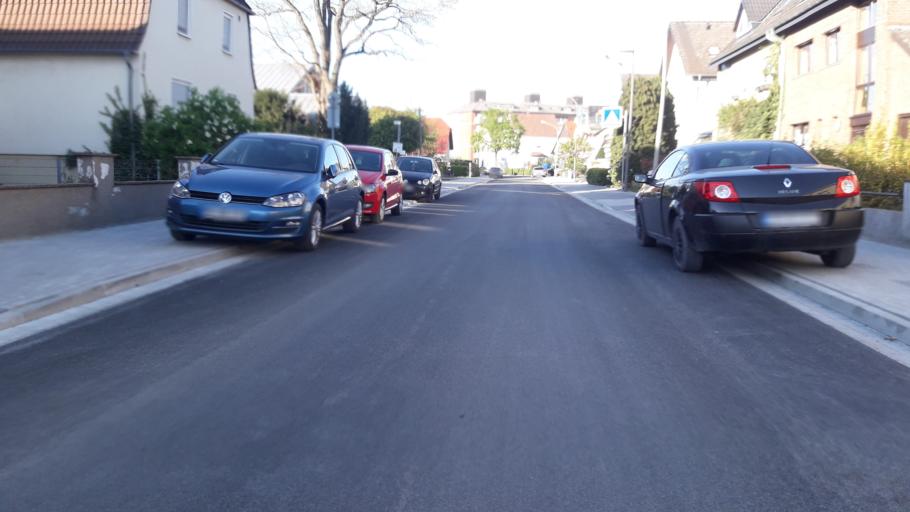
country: DE
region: North Rhine-Westphalia
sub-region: Regierungsbezirk Detmold
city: Paderborn
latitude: 51.7362
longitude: 8.7603
